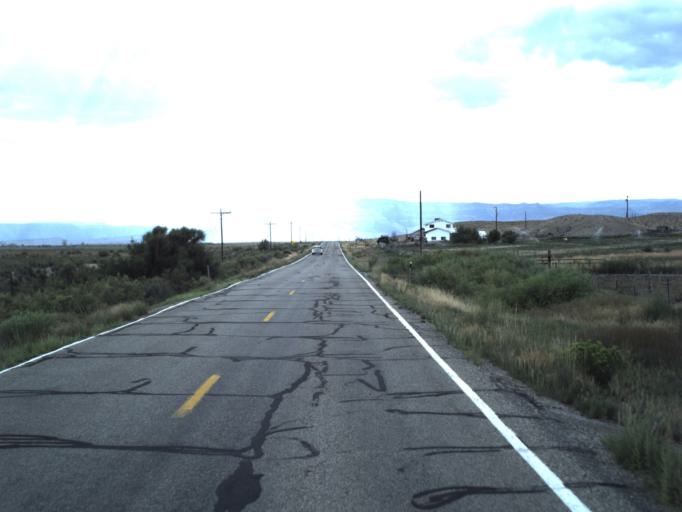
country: US
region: Utah
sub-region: Emery County
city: Huntington
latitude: 39.3460
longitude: -110.8854
